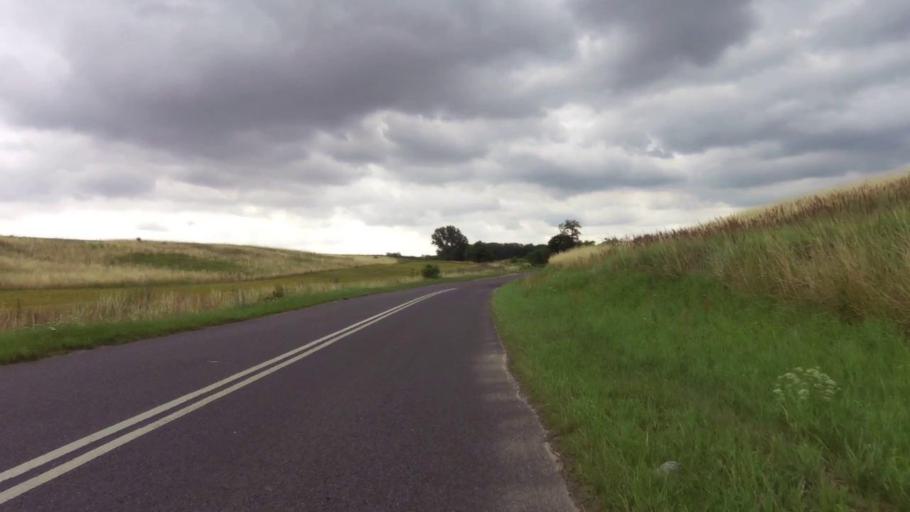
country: PL
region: West Pomeranian Voivodeship
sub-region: Powiat gryfinski
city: Cedynia
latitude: 52.8742
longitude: 14.2186
